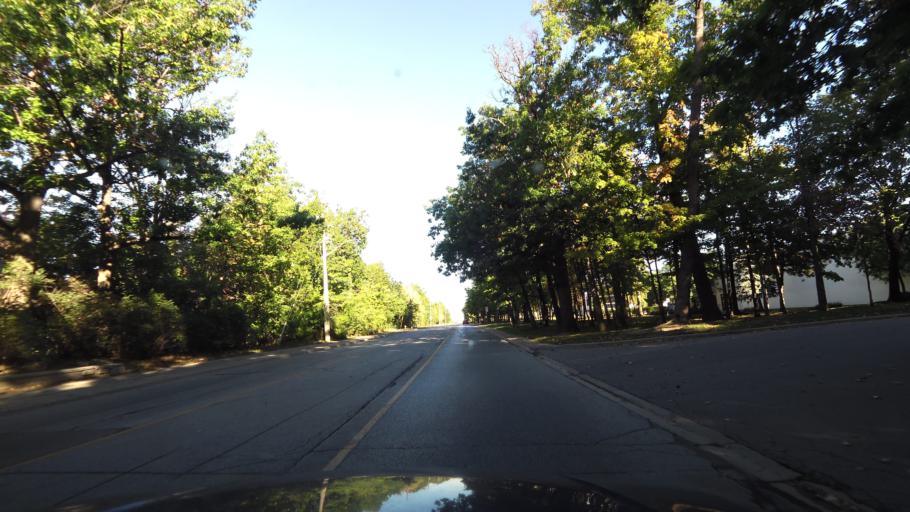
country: CA
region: Ontario
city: Mississauga
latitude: 43.6091
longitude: -79.6797
